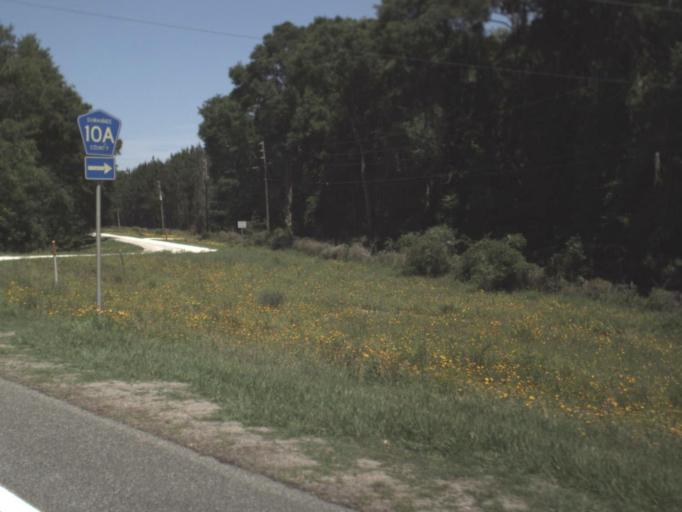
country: US
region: Florida
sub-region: Suwannee County
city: Wellborn
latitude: 30.2038
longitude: -82.7977
